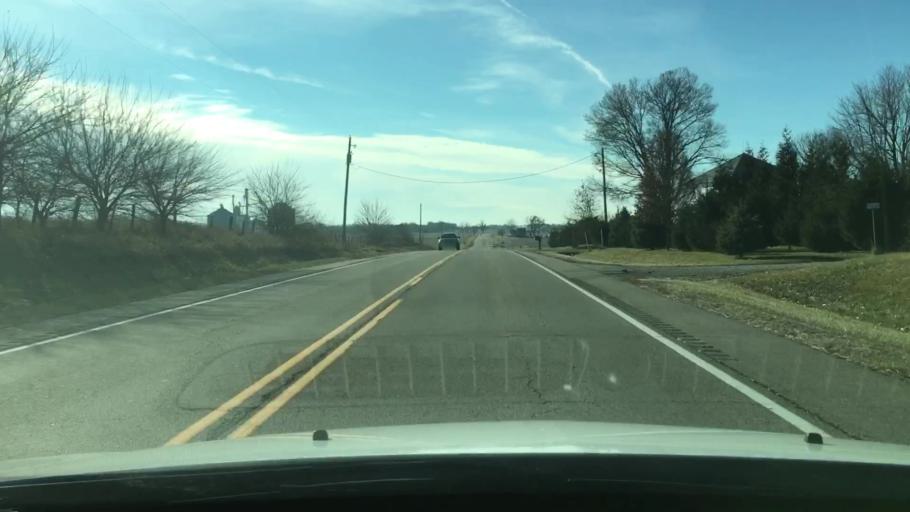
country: US
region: Illinois
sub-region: Woodford County
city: Washburn
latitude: 40.8837
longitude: -89.3150
